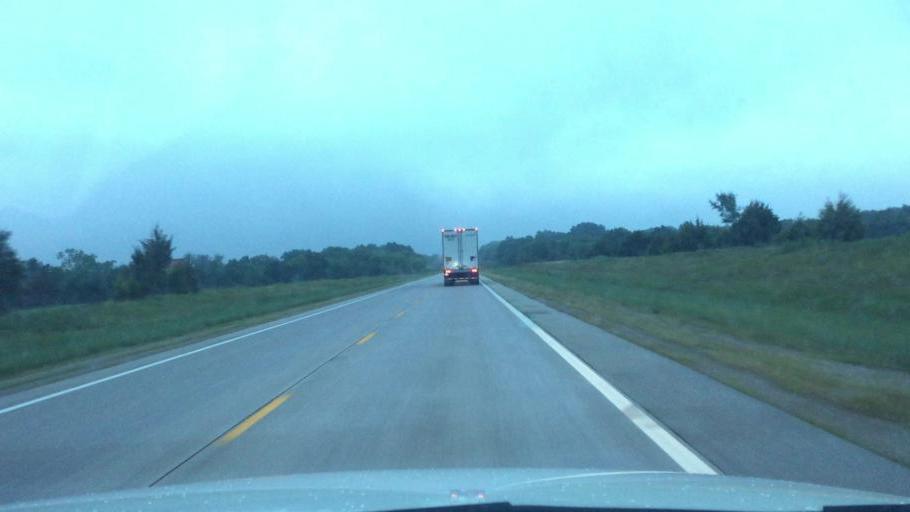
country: US
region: Kansas
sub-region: Neosho County
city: Chanute
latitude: 37.6270
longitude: -95.4796
